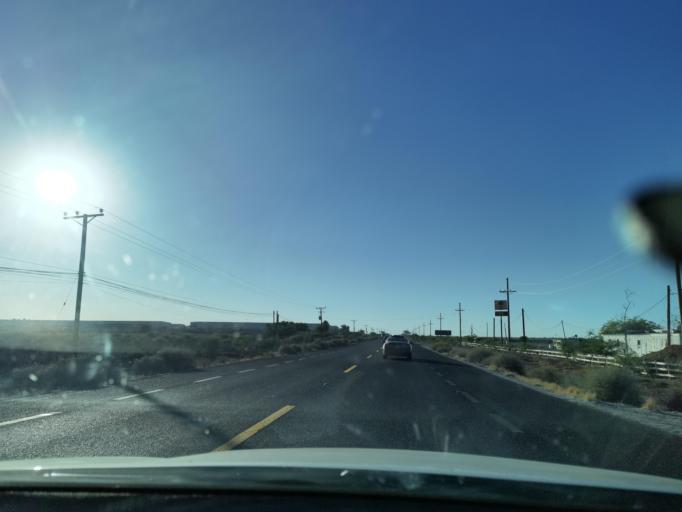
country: MX
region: Baja California
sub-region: Mexicali
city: Islas Agrarias Grupo A
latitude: 32.6374
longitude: -115.2867
